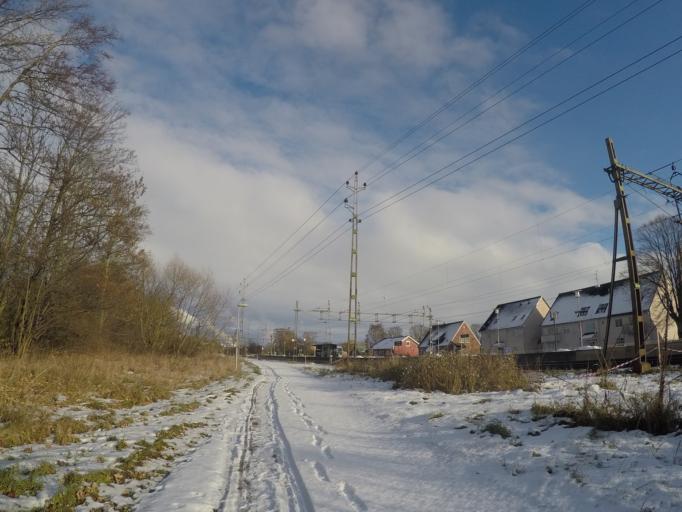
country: SE
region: Skane
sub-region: Lunds Kommun
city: Lund
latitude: 55.7784
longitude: 13.2412
